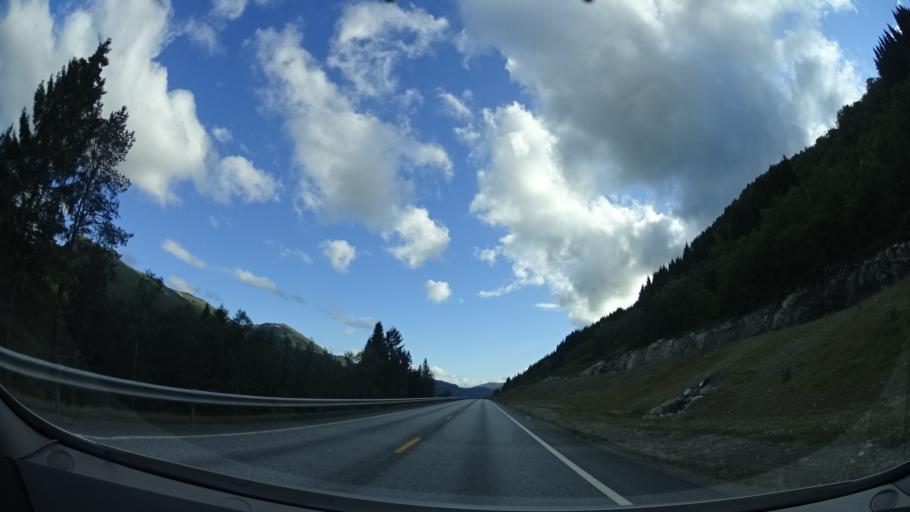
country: NO
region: More og Romsdal
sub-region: Gjemnes
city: Batnfjordsora
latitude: 62.9188
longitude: 7.6961
